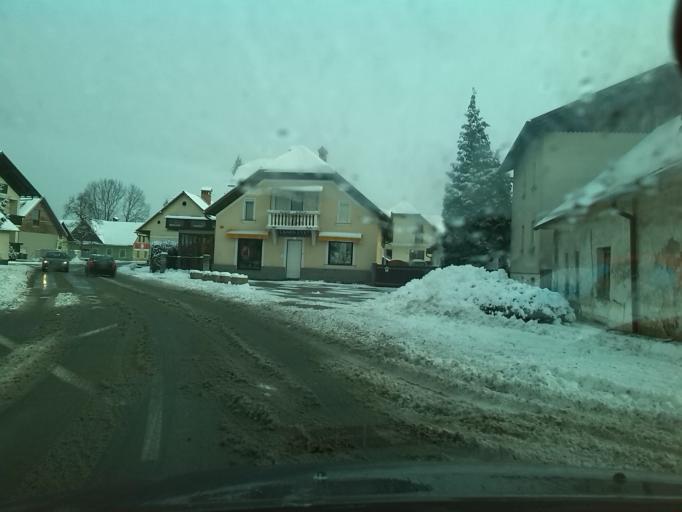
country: SI
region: Komenda
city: Moste
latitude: 46.1950
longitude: 14.5490
